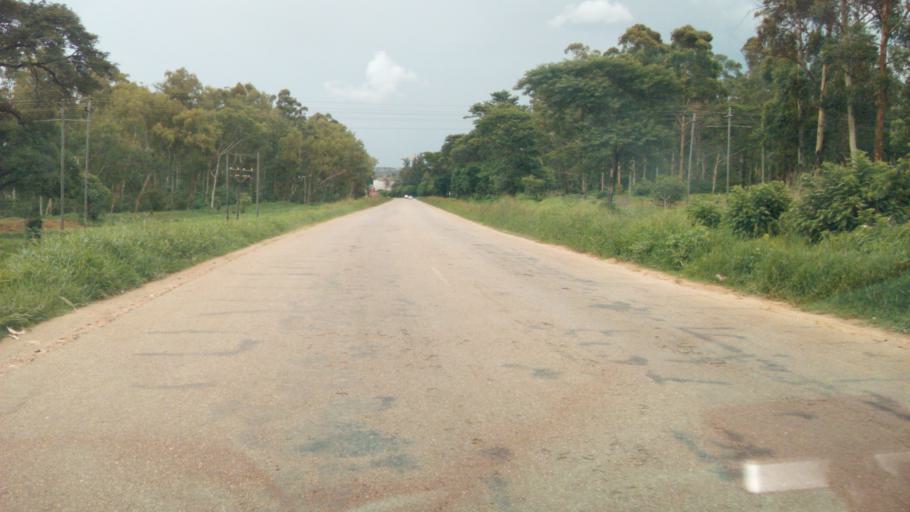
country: ZW
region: Mashonaland Central
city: Bindura
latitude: -17.3042
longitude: 31.3166
